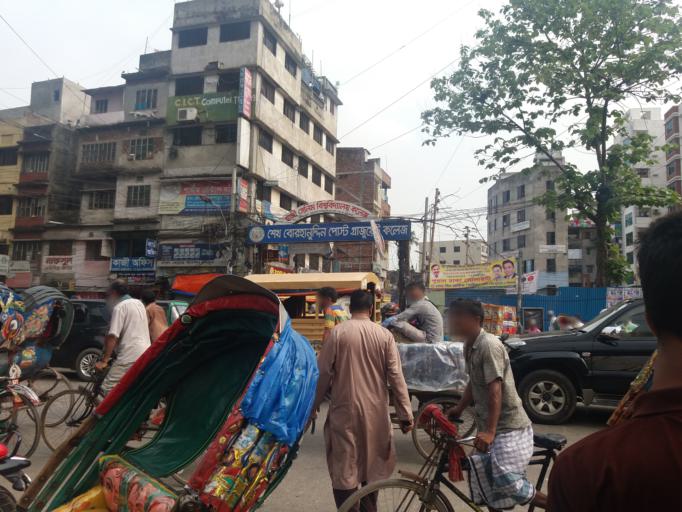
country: BD
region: Dhaka
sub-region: Dhaka
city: Dhaka
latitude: 23.7241
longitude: 90.4003
